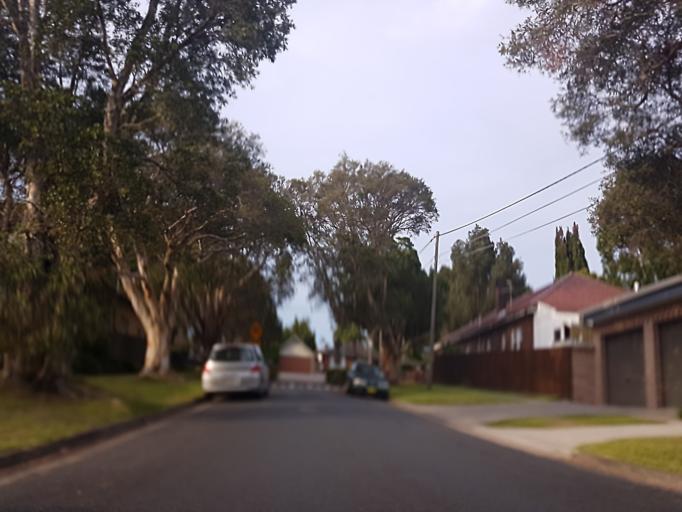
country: AU
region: New South Wales
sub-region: Willoughby
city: Castle Cove
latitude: -33.8048
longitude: 151.2034
